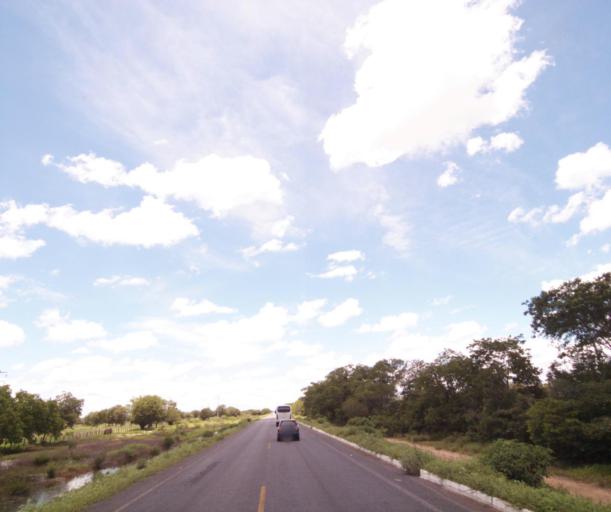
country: BR
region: Bahia
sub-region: Bom Jesus Da Lapa
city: Bom Jesus da Lapa
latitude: -13.2597
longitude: -43.4951
